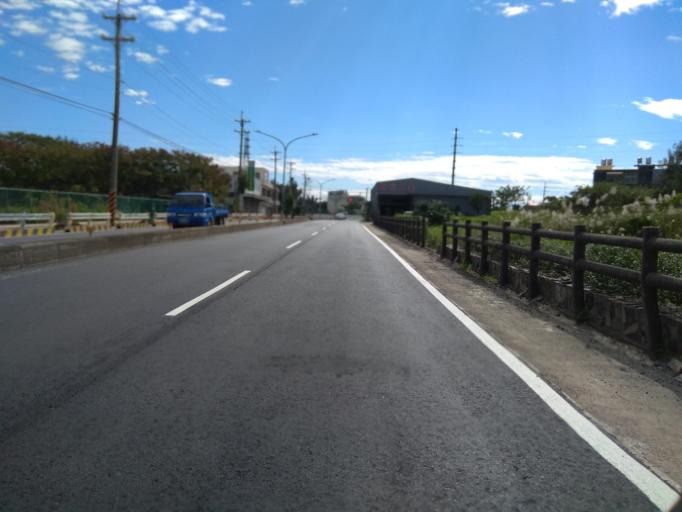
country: TW
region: Taiwan
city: Taoyuan City
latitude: 25.0566
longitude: 121.1374
